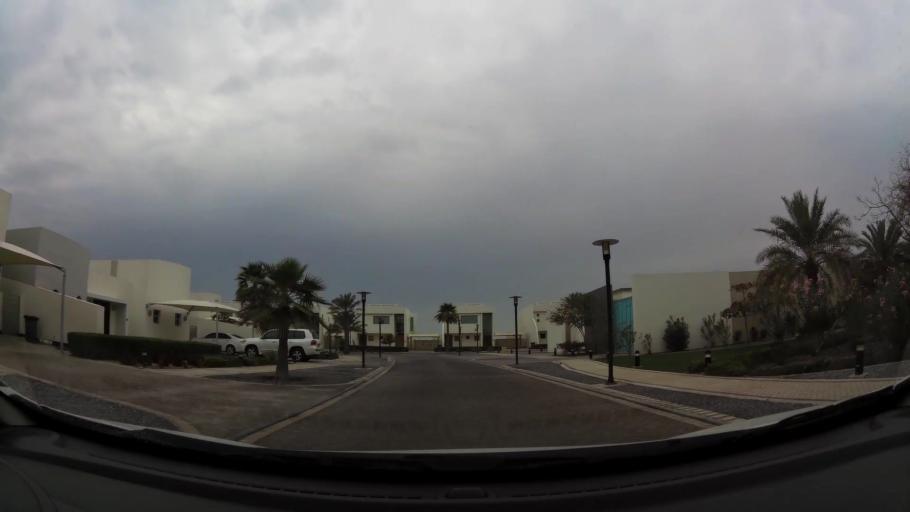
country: BH
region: Central Governorate
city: Dar Kulayb
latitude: 25.8441
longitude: 50.6120
